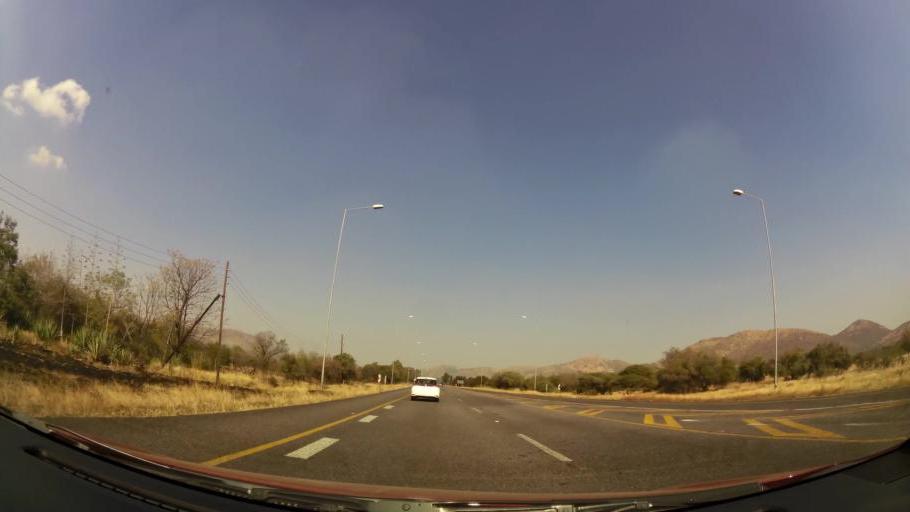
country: ZA
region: North-West
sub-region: Bojanala Platinum District Municipality
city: Rustenburg
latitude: -25.6193
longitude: 27.1556
